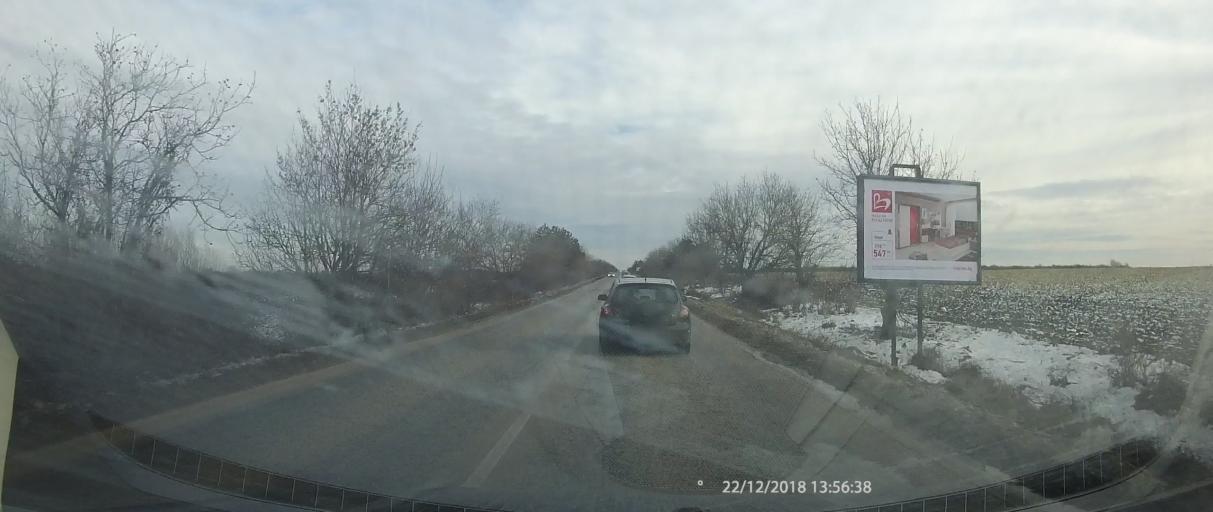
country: BG
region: Pleven
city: Iskur
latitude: 43.3390
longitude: 24.3063
